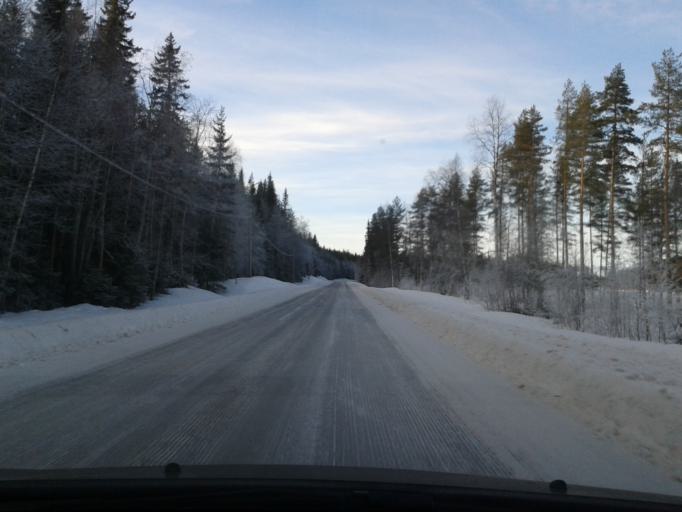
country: SE
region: Vaesternorrland
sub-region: OErnskoeldsviks Kommun
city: Bredbyn
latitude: 63.6580
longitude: 17.8640
